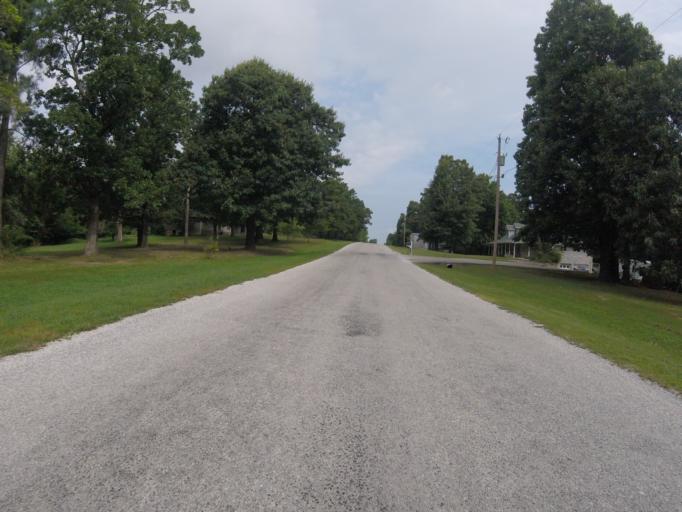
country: US
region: Arkansas
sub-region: Washington County
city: Farmington
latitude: 36.0881
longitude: -94.3018
